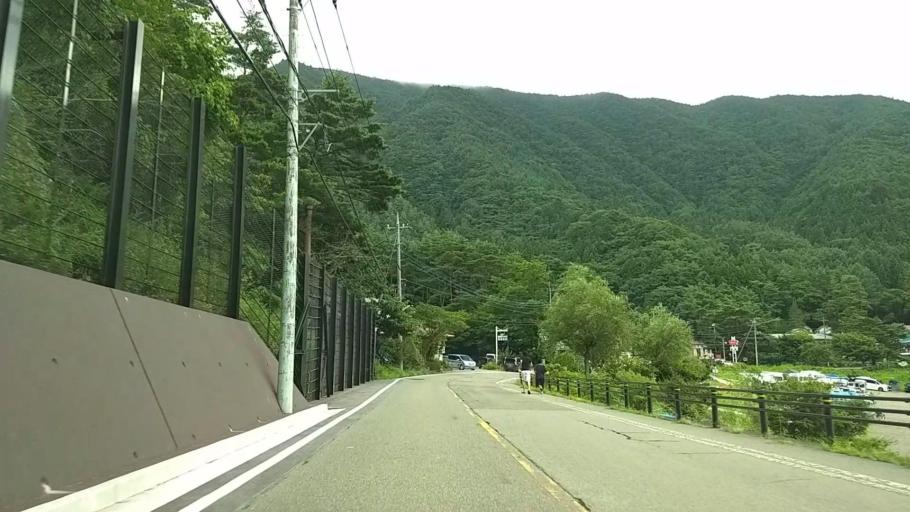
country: JP
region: Yamanashi
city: Fujikawaguchiko
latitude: 35.5012
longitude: 138.6989
